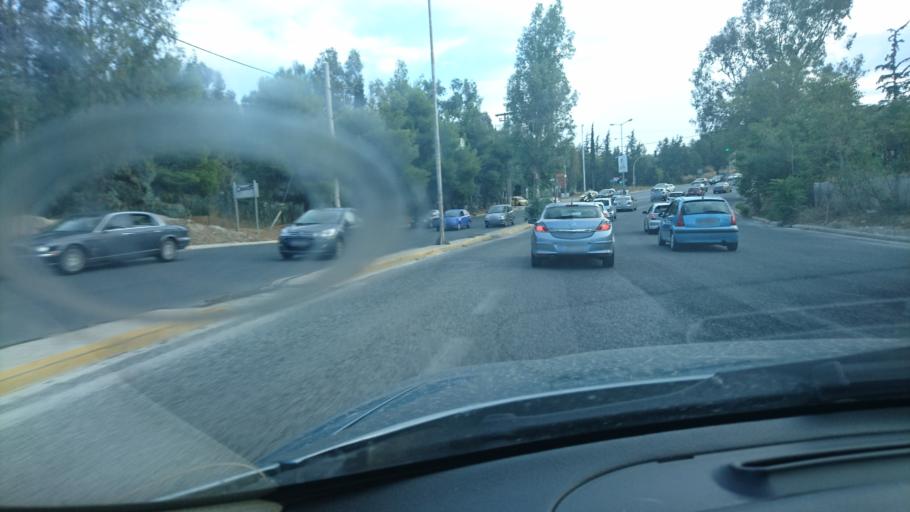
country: GR
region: Attica
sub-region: Nomarchia Athinas
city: Kaisariani
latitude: 37.9569
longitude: 23.7750
